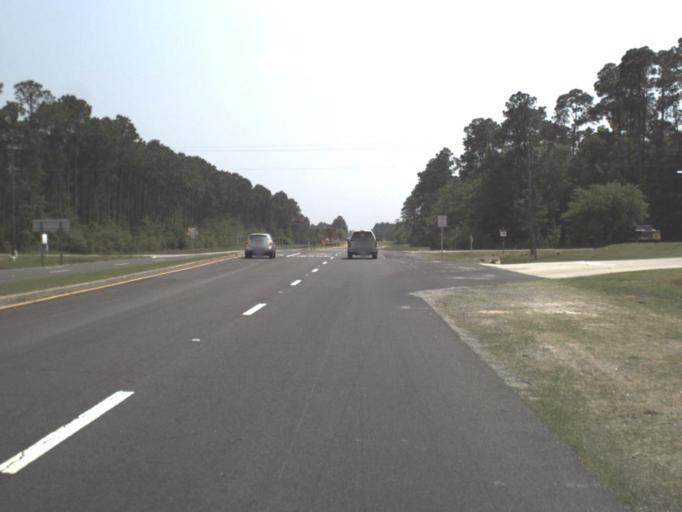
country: US
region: Florida
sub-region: Santa Rosa County
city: Bagdad
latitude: 30.5327
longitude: -87.0874
